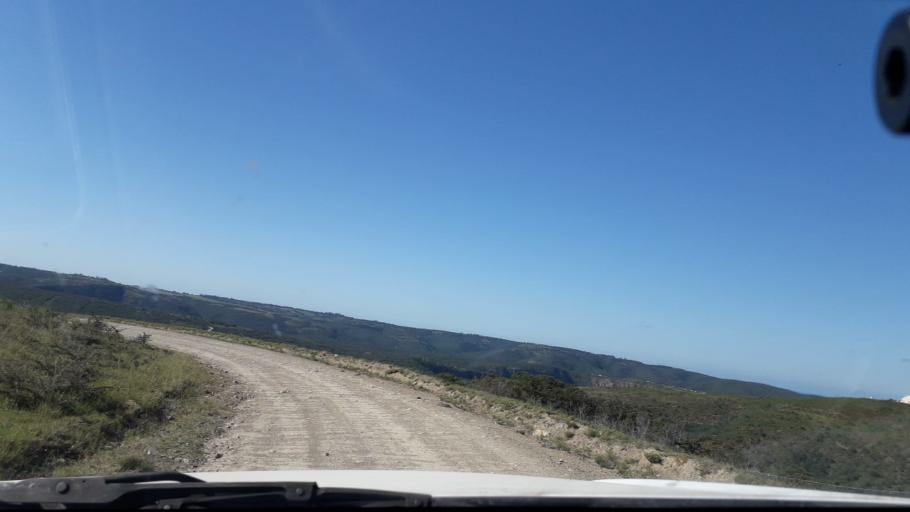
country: ZA
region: Eastern Cape
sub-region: Amathole District Municipality
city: Komga
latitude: -32.7862
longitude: 27.9551
